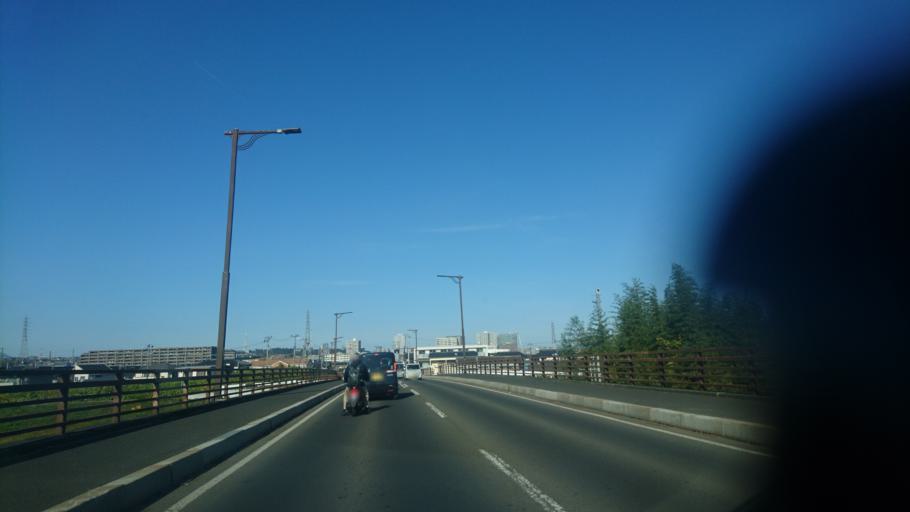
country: JP
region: Miyagi
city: Sendai
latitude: 38.2078
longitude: 140.8848
